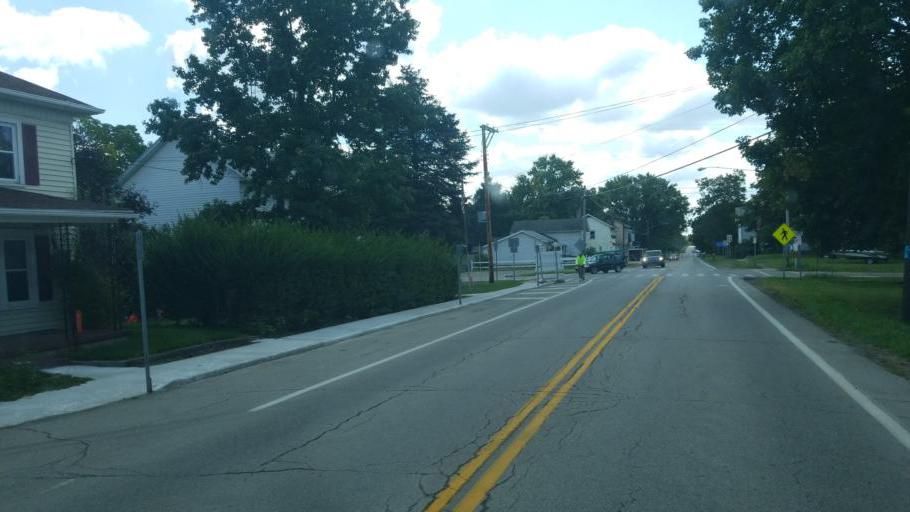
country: US
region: Ohio
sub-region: Ashland County
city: Ashland
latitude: 40.9222
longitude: -82.2816
